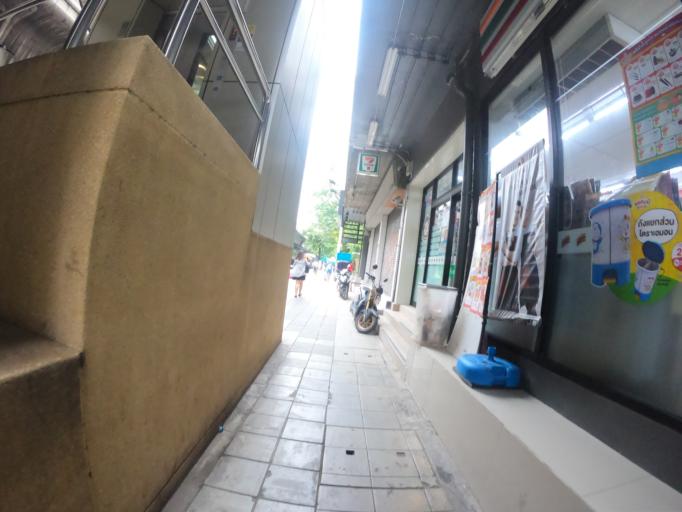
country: TH
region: Bangkok
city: Chatuchak
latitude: 13.8395
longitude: 100.5516
